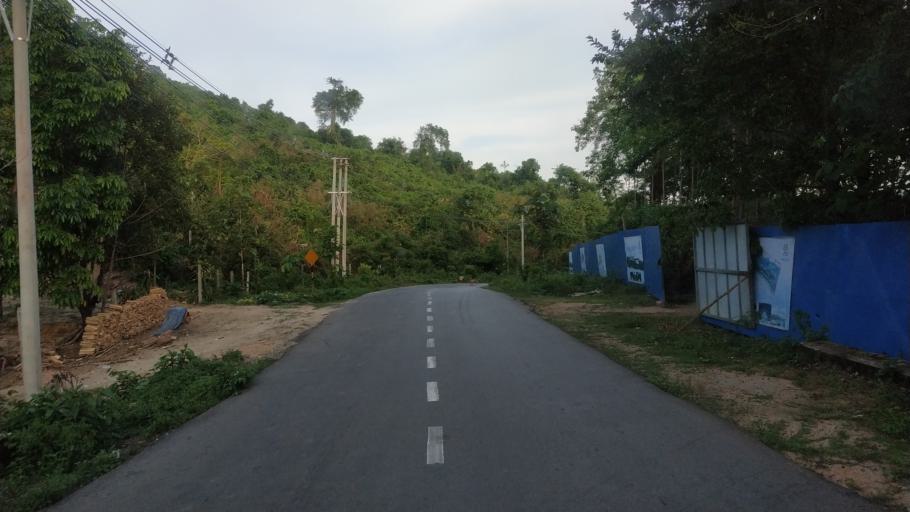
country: MM
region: Mon
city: Kyaikto
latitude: 17.4163
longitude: 97.0710
